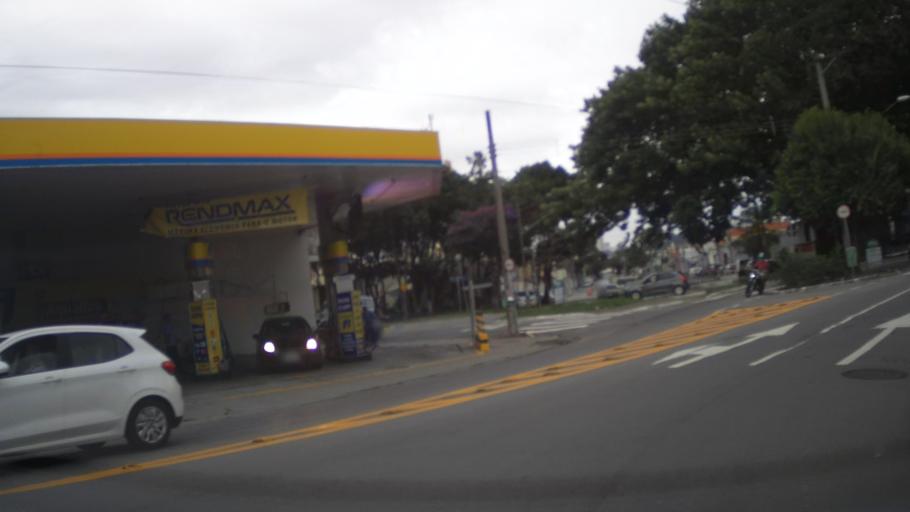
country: BR
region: Sao Paulo
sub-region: Guarulhos
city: Guarulhos
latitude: -23.4614
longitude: -46.5586
